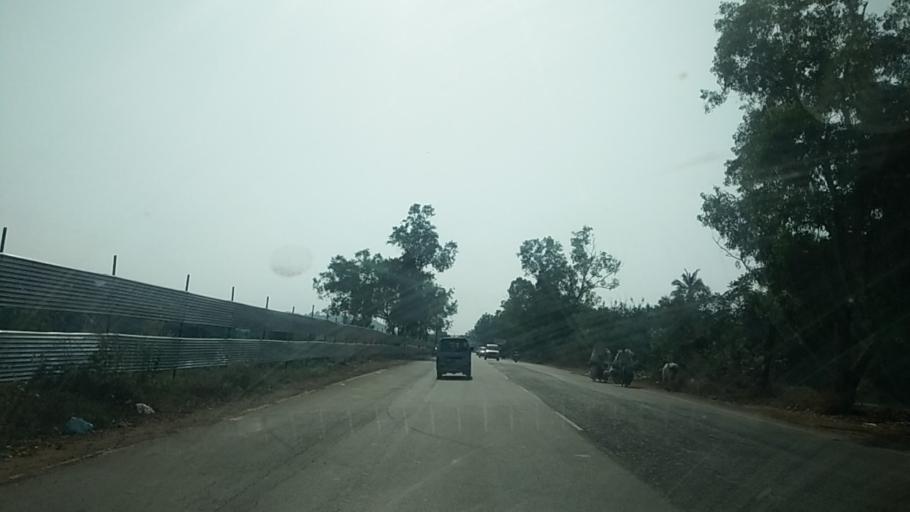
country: IN
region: Goa
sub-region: North Goa
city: Guirim
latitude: 15.5767
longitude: 73.8095
